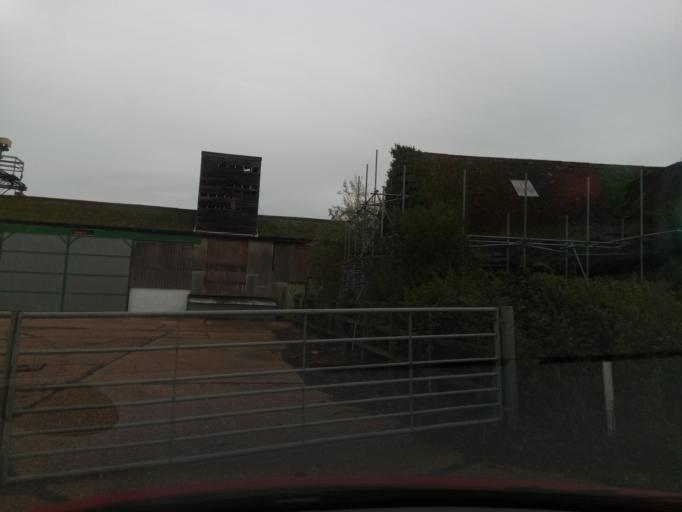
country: GB
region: England
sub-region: Essex
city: West Mersea
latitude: 51.8083
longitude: 0.8980
